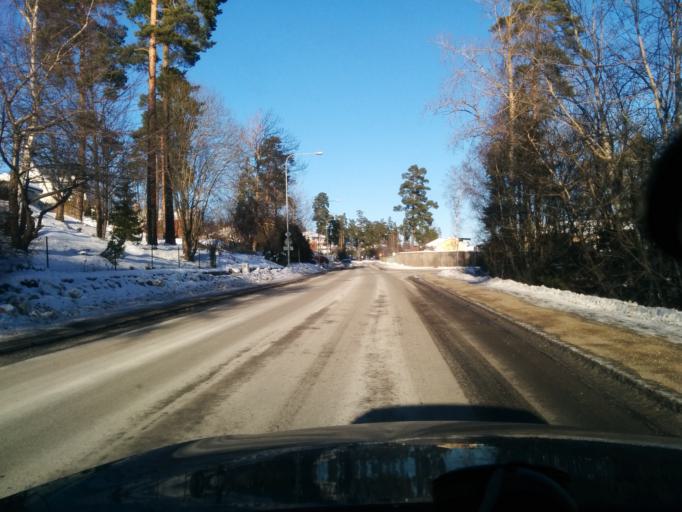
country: SE
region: Stockholm
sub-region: Taby Kommun
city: Taby
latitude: 59.4638
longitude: 18.0875
